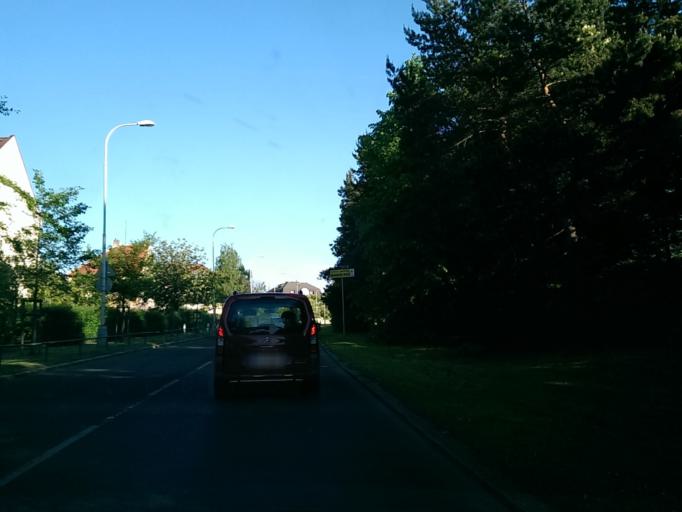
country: CZ
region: Praha
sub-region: Praha 8
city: Karlin
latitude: 50.0446
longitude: 14.4861
